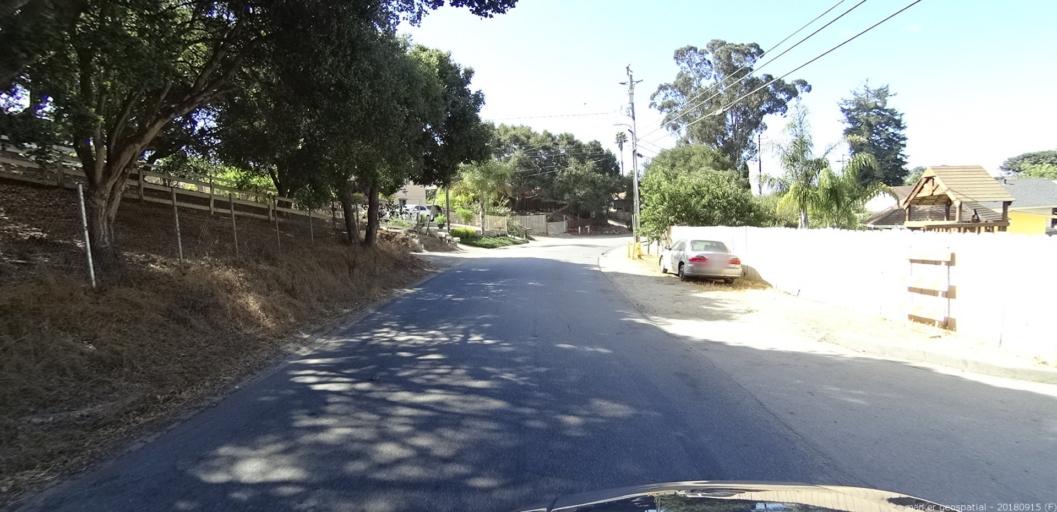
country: US
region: California
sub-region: Monterey County
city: Las Lomas
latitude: 36.8743
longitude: -121.7350
